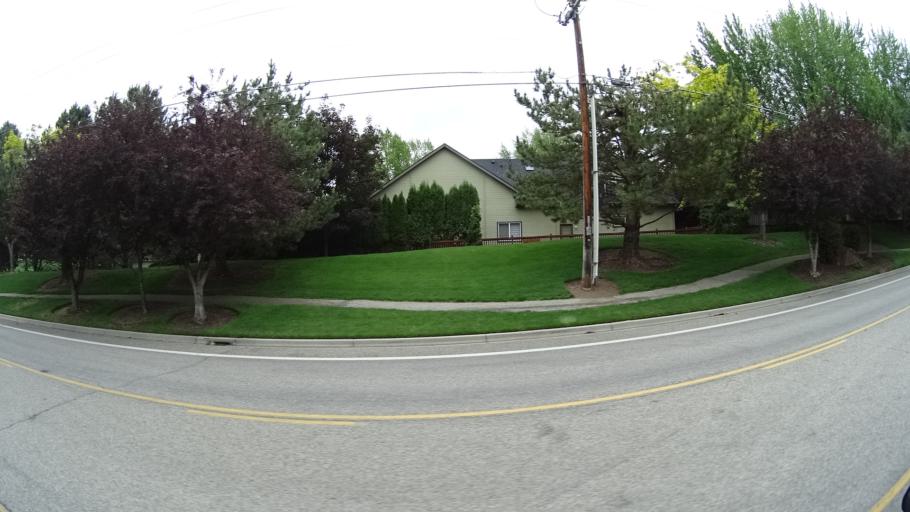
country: US
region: Idaho
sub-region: Ada County
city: Eagle
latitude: 43.7065
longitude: -116.3267
